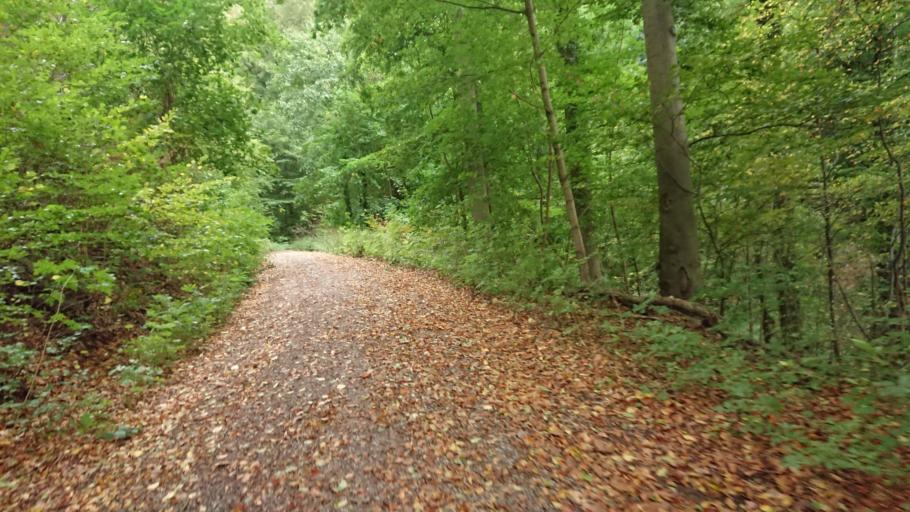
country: DE
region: Lower Saxony
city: Bovenden
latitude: 51.6044
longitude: 9.9516
